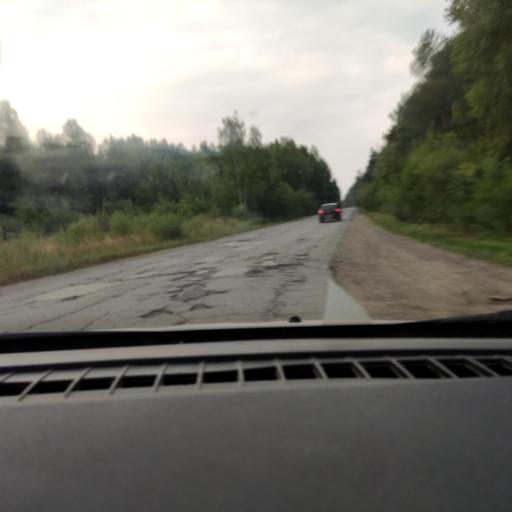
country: RU
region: Perm
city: Perm
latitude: 58.1084
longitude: 56.2827
